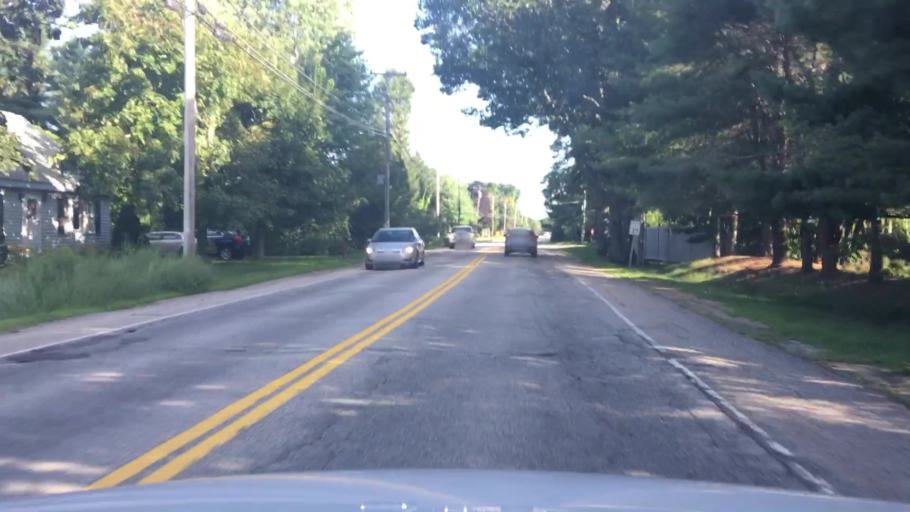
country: US
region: Maine
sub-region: Cumberland County
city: Scarborough
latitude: 43.5748
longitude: -70.3193
